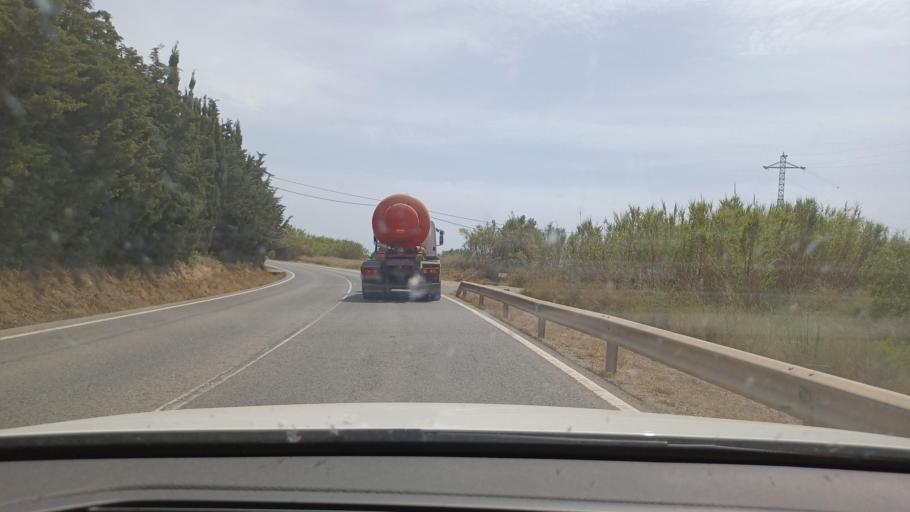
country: ES
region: Catalonia
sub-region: Provincia de Tarragona
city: Cambrils
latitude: 41.1011
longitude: 1.0827
